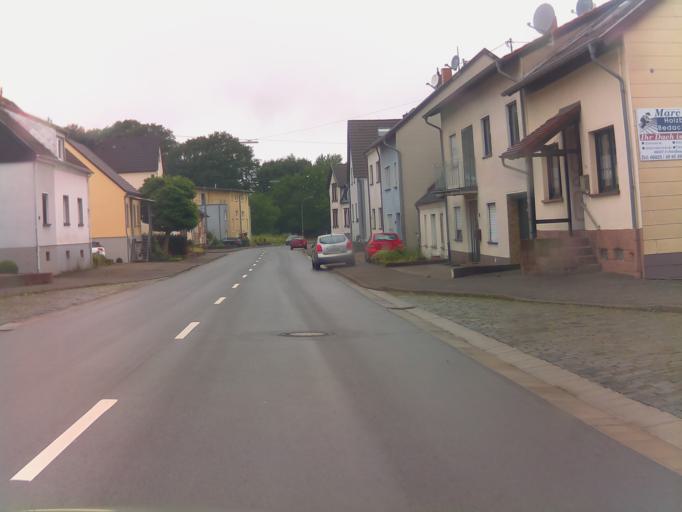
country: DE
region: Saarland
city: Heusweiler
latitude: 49.3308
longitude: 6.9755
